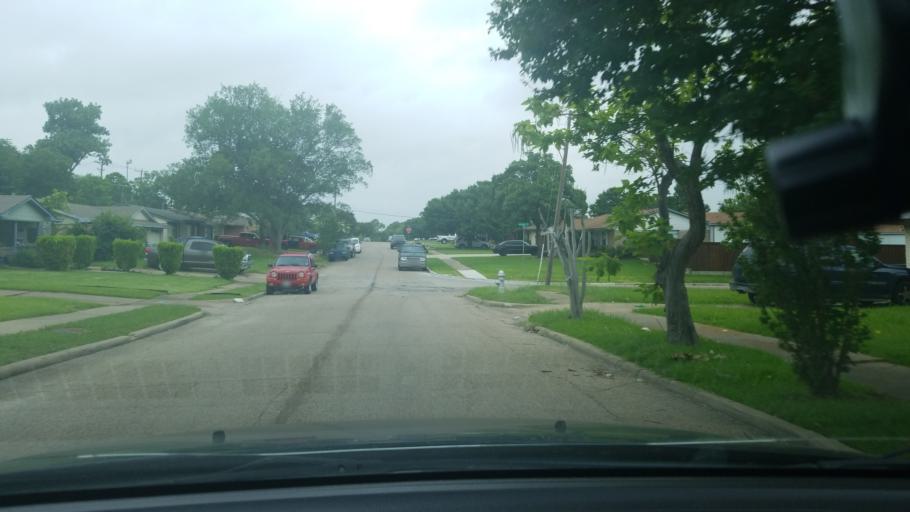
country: US
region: Texas
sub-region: Dallas County
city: Mesquite
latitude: 32.7842
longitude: -96.6357
